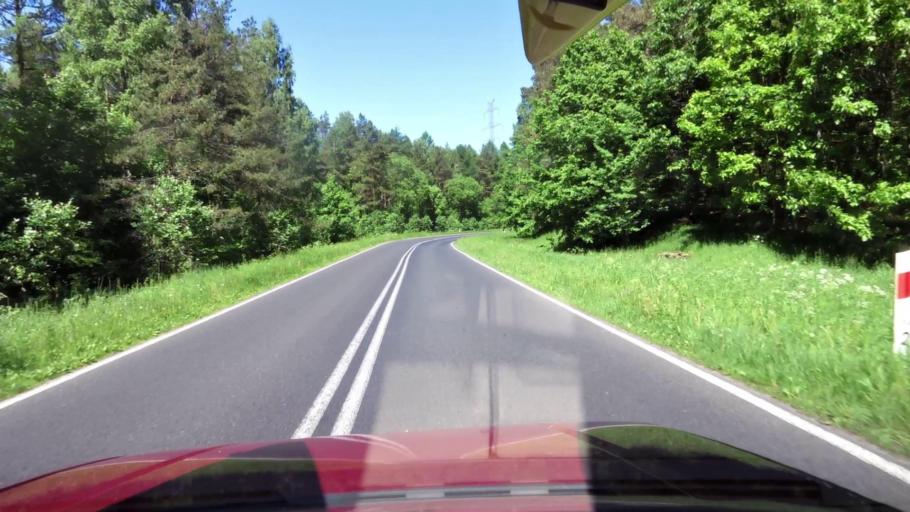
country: PL
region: West Pomeranian Voivodeship
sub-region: Powiat koszalinski
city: Polanow
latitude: 54.0289
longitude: 16.7205
